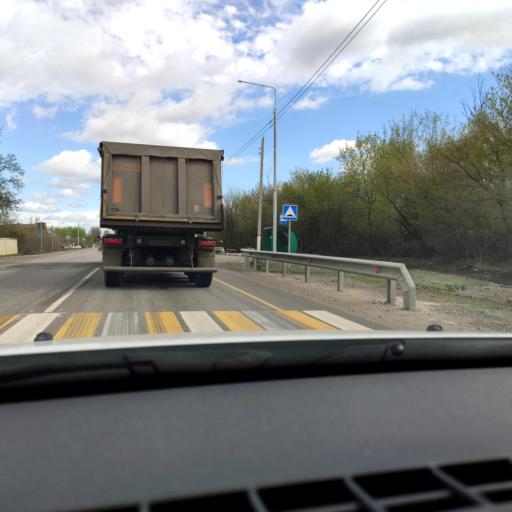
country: RU
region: Lipetsk
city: Yelets
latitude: 52.5584
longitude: 38.6936
